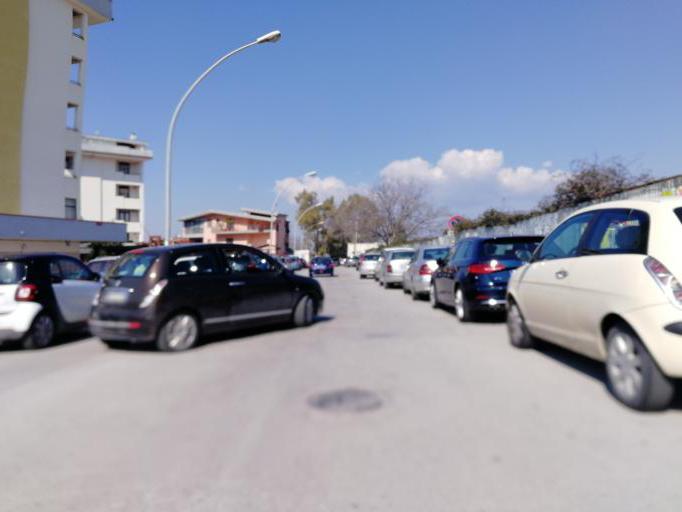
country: IT
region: Campania
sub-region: Provincia di Caserta
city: Santa Maria Capua Vetere
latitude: 41.0904
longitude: 14.2578
